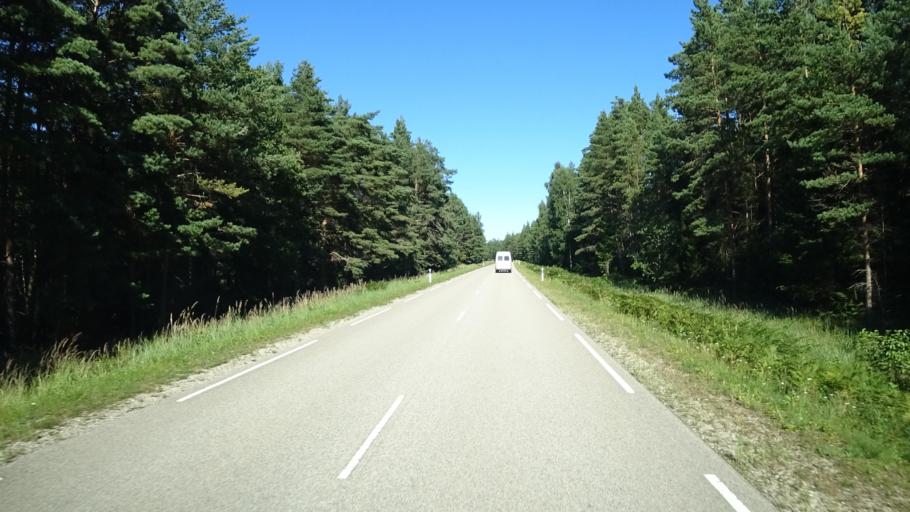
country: LV
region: Dundaga
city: Dundaga
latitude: 57.7439
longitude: 22.5541
